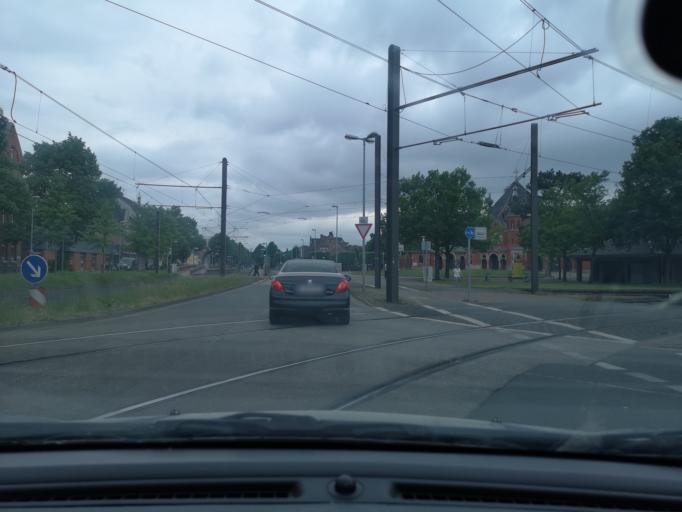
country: DE
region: Lower Saxony
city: Hannover
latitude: 52.3998
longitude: 9.6703
